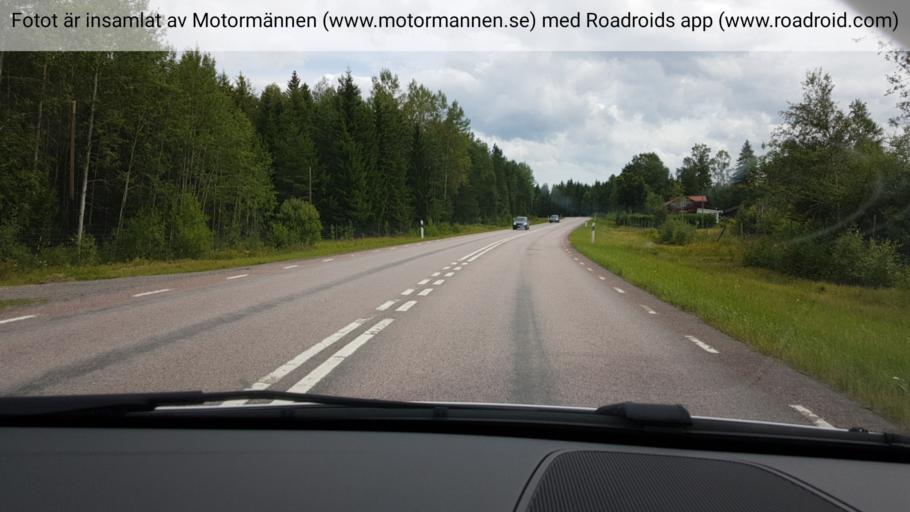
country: SE
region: Uppsala
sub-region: Osthammars Kommun
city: OEsthammar
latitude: 60.2418
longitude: 18.3142
